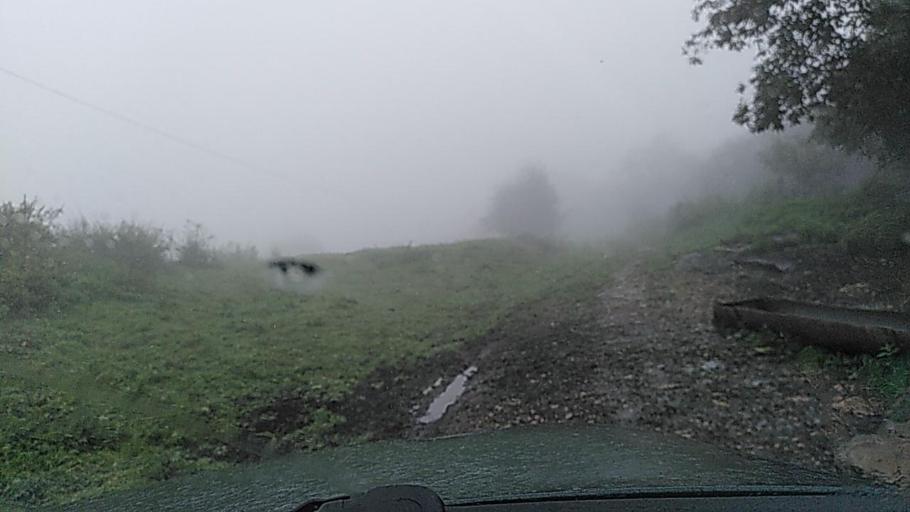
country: RU
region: Kabardino-Balkariya
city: Belaya Rechka
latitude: 43.3561
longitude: 43.3990
